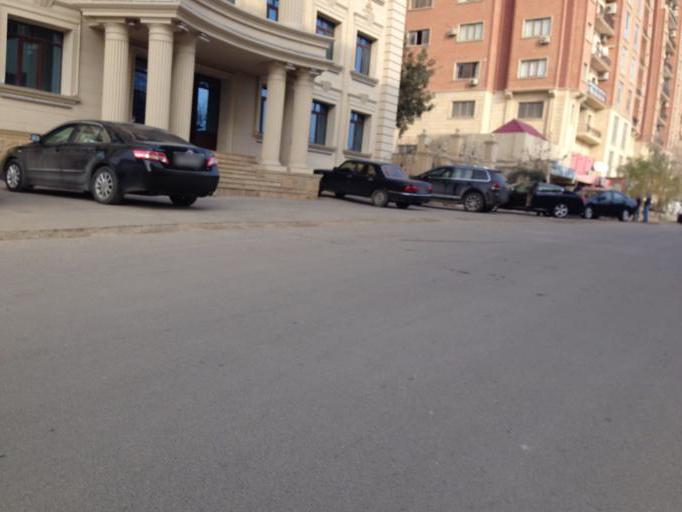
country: AZ
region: Baki
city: Baku
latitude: 40.3981
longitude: 49.8608
